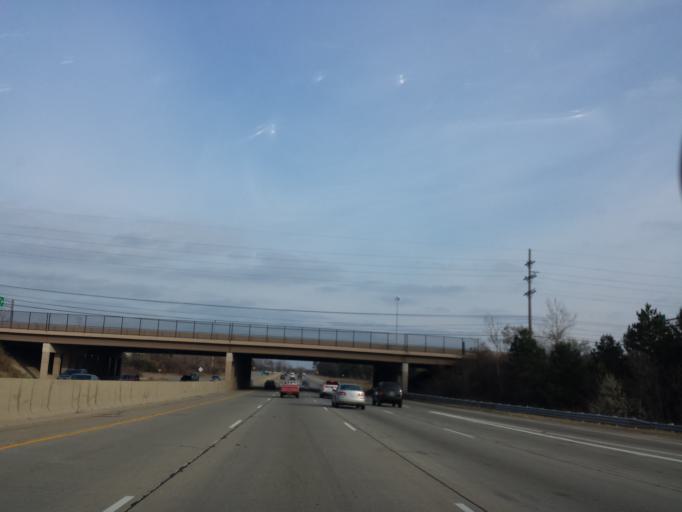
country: US
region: Michigan
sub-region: Oakland County
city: Farmington Hills
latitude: 42.4960
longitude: -83.3599
